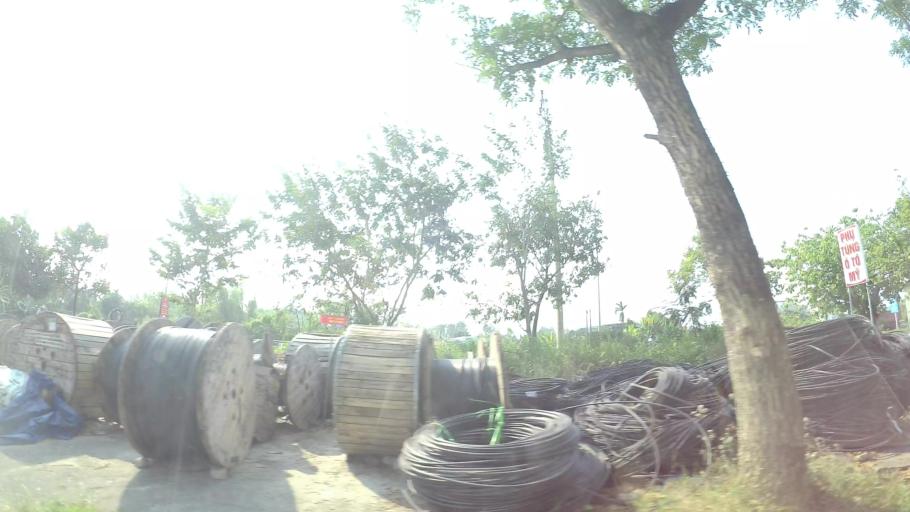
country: VN
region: Da Nang
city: Cam Le
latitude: 16.0067
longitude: 108.1921
